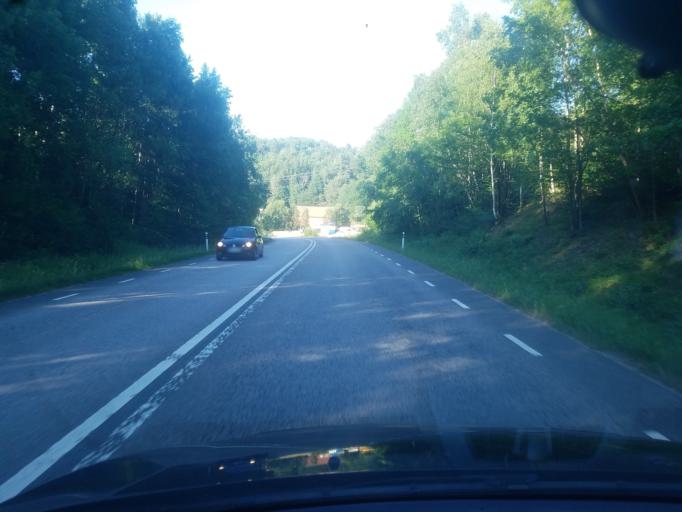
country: SE
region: Vaestra Goetaland
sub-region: Orust
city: Henan
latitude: 58.2461
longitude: 11.6867
